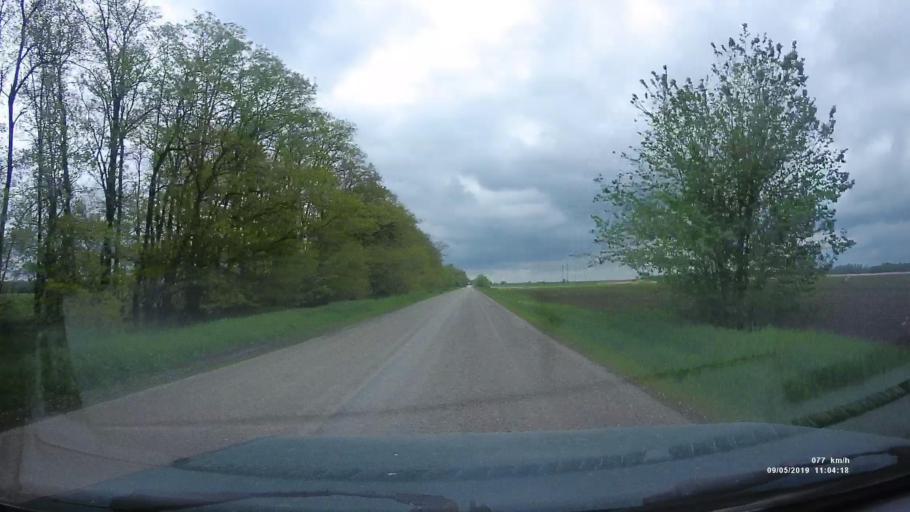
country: RU
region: Krasnodarskiy
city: Kanelovskaya
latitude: 46.8188
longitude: 39.2100
